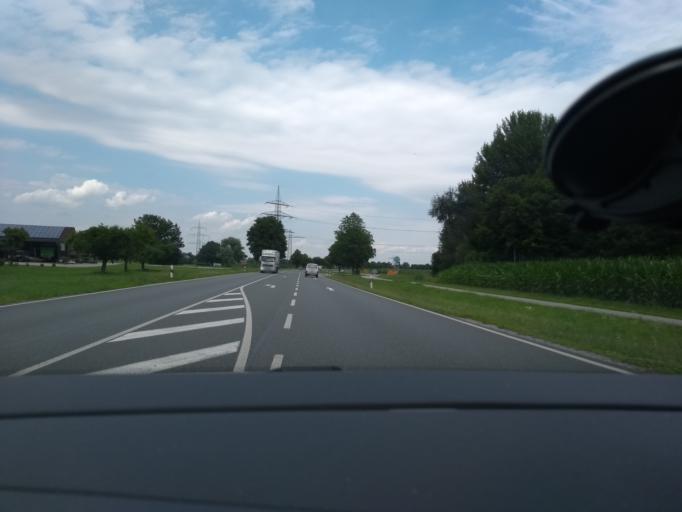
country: DE
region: Bavaria
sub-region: Upper Bavaria
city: Schechen
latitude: 47.9125
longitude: 12.1275
